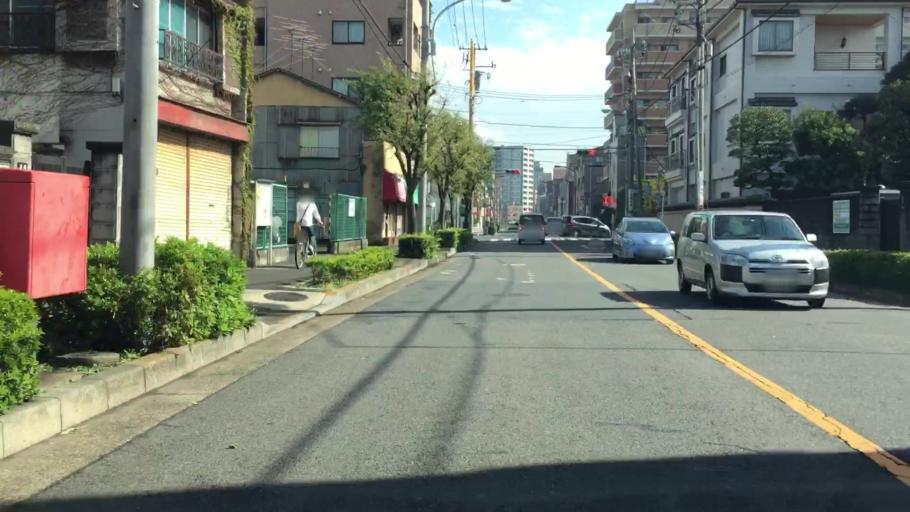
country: JP
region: Saitama
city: Yashio-shi
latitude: 35.7629
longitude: 139.8409
